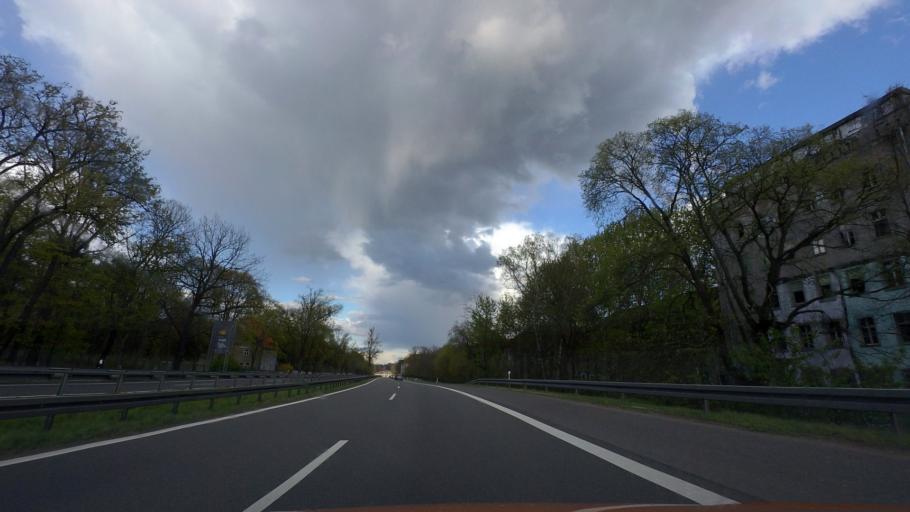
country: DE
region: Brandenburg
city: Brieselang
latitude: 52.5330
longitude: 13.0049
